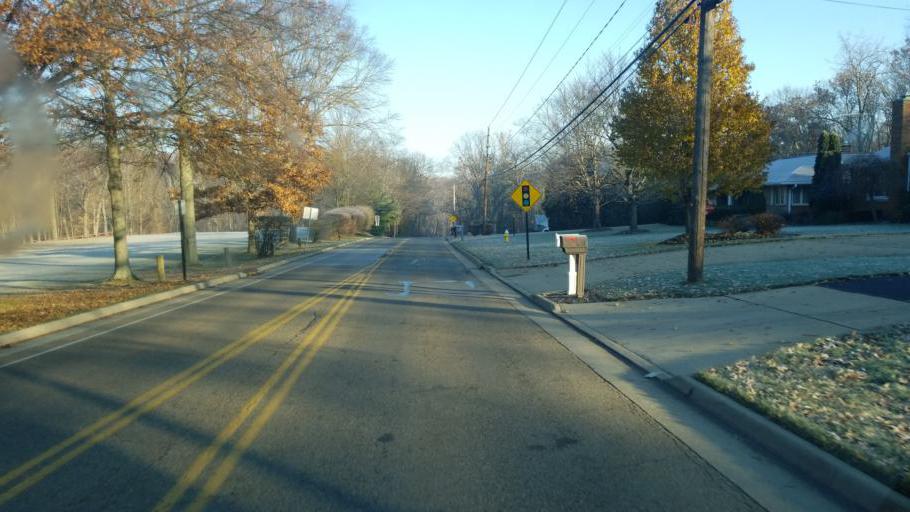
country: US
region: Ohio
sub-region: Summit County
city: Fairlawn
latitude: 41.1303
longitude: -81.5875
